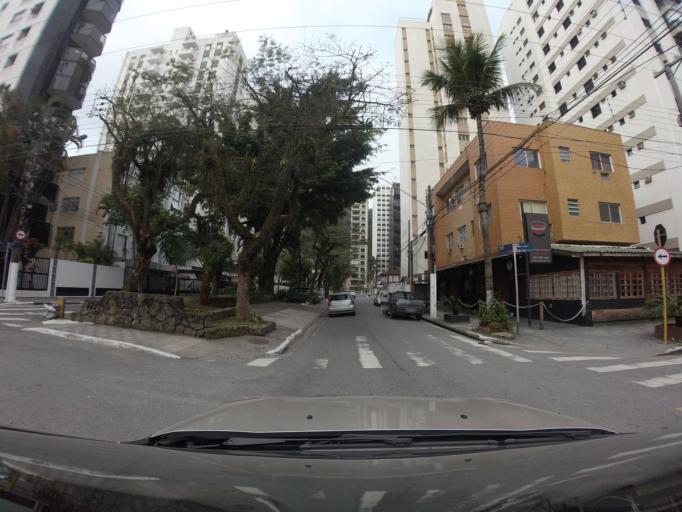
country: BR
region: Sao Paulo
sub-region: Guaruja
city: Guaruja
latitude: -23.9938
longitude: -46.2548
